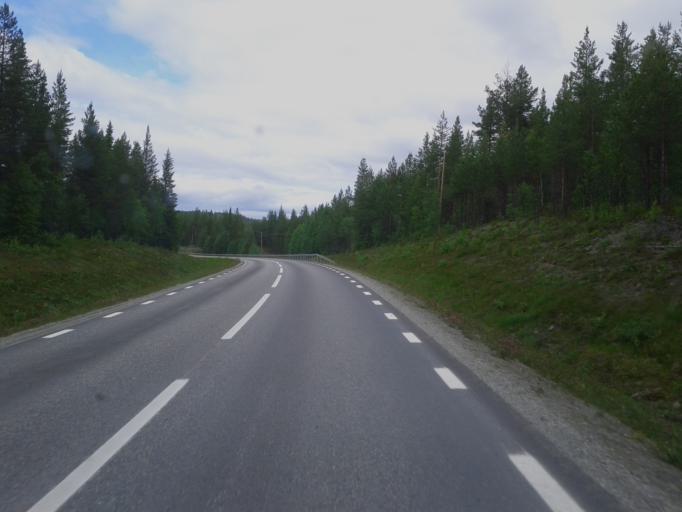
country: SE
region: Vaesterbotten
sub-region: Storumans Kommun
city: Fristad
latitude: 65.3797
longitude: 16.5134
